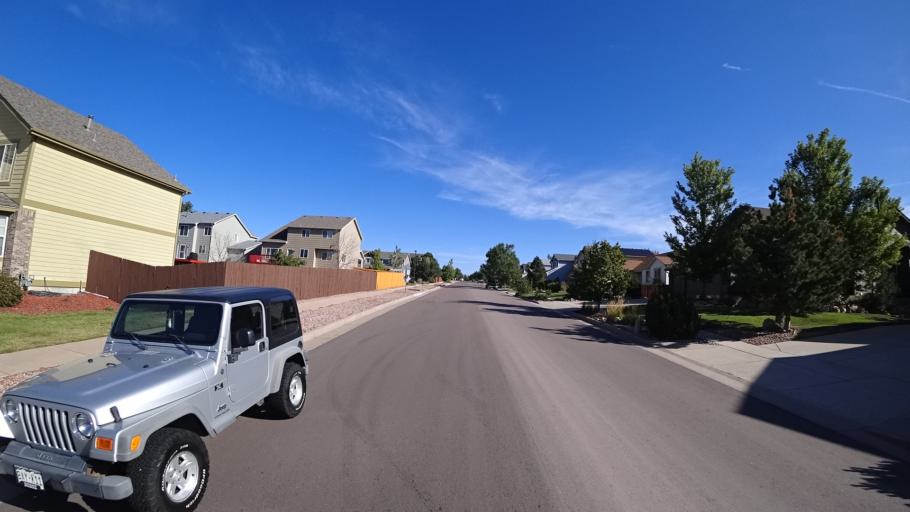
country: US
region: Colorado
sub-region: El Paso County
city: Black Forest
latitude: 38.9436
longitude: -104.7386
